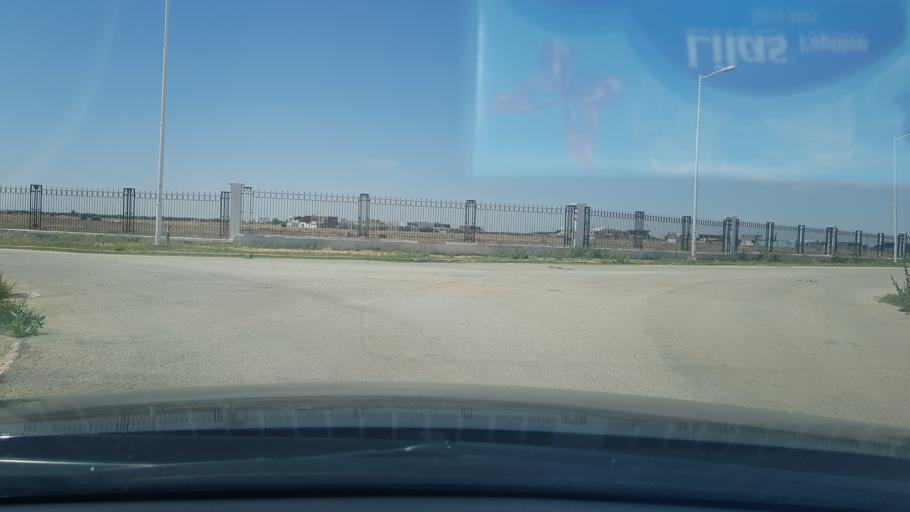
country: TN
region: Safaqis
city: Al Qarmadah
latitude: 34.8355
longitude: 10.7531
